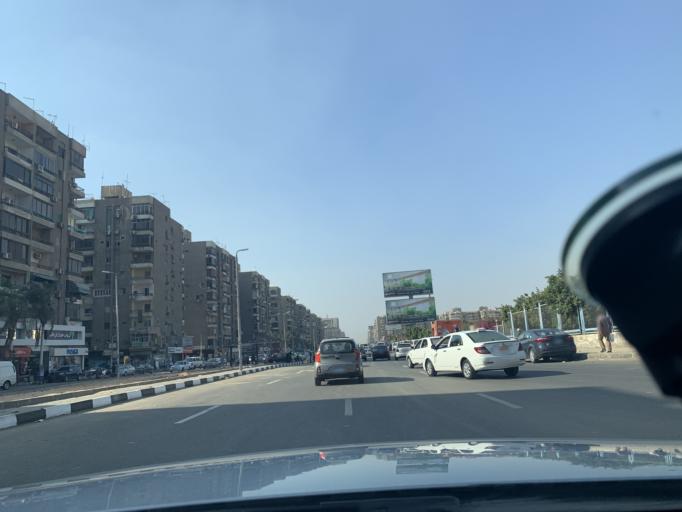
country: EG
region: Muhafazat al Qahirah
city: Cairo
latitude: 30.0694
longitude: 31.3385
